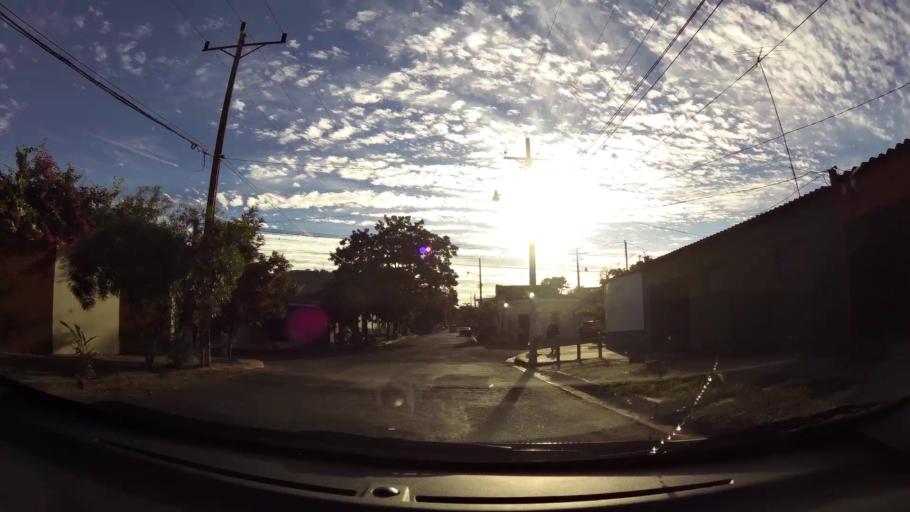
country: SV
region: Santa Ana
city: Santa Ana
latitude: 13.9928
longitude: -89.5489
